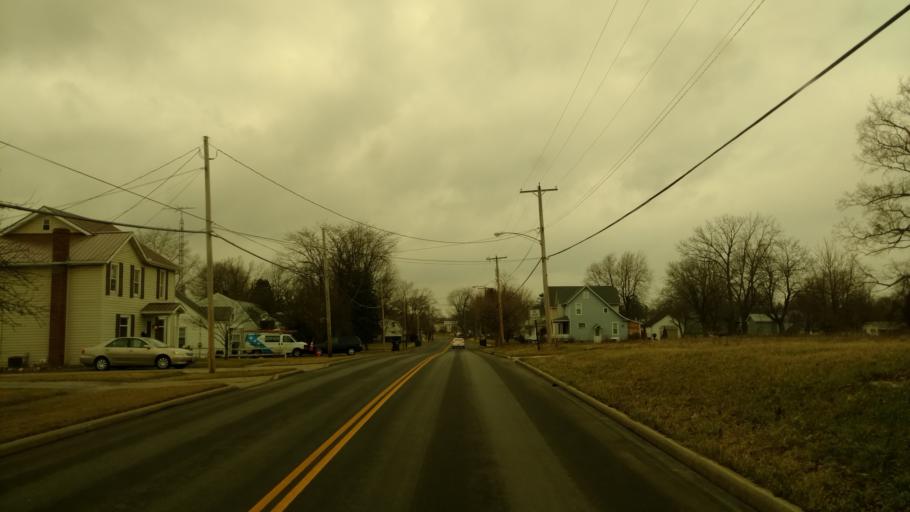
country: US
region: Ohio
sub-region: Richland County
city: Shelby
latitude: 40.8805
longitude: -82.6460
